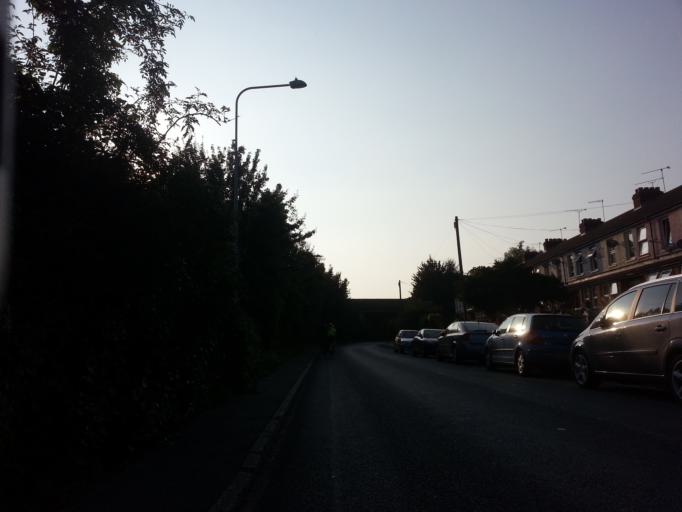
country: GB
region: England
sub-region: Suffolk
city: Bramford
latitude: 52.0698
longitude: 1.1124
